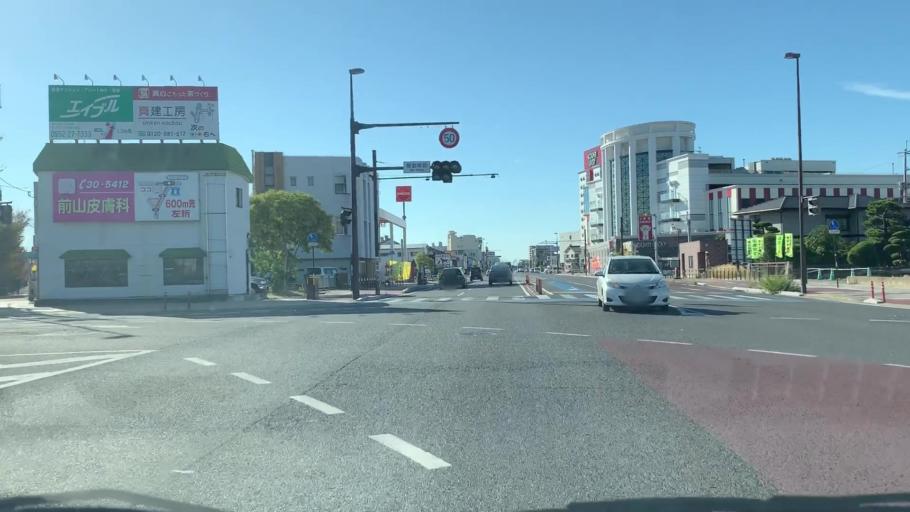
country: JP
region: Saga Prefecture
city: Saga-shi
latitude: 33.2723
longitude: 130.2941
